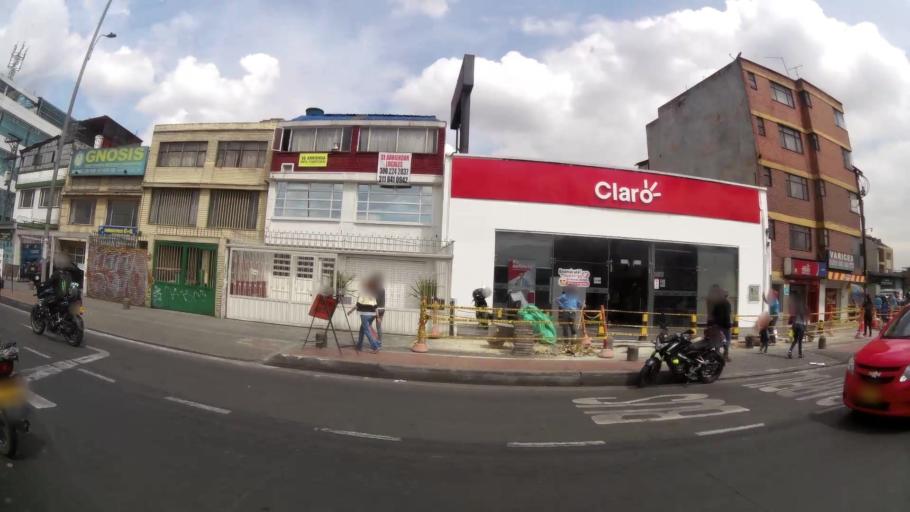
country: CO
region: Bogota D.C.
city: Bogota
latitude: 4.6032
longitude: -74.1012
